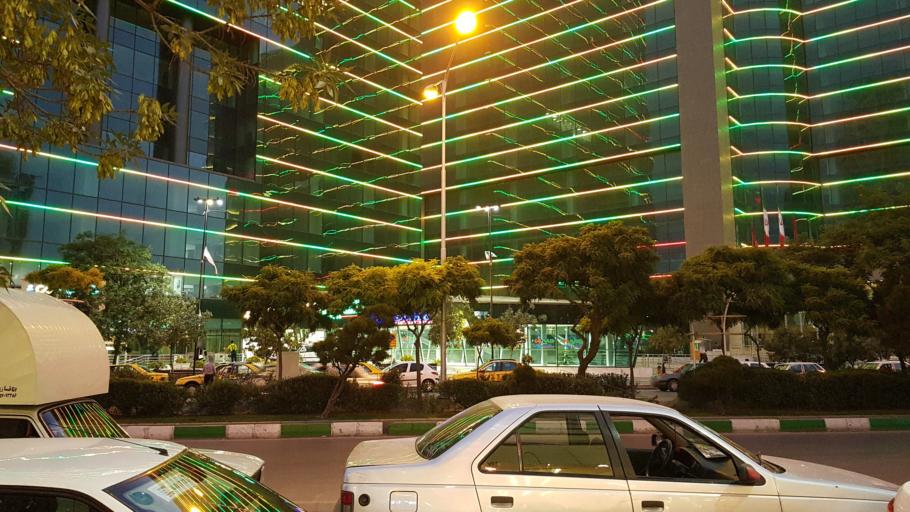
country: IR
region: Razavi Khorasan
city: Mashhad
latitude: 36.3261
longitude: 59.5636
